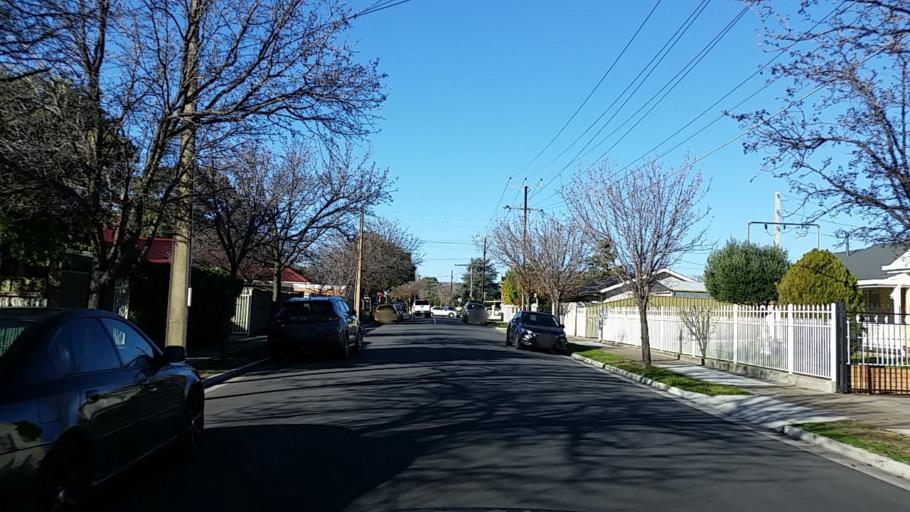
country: AU
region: South Australia
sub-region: City of West Torrens
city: Plympton
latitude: -34.9567
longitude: 138.5531
